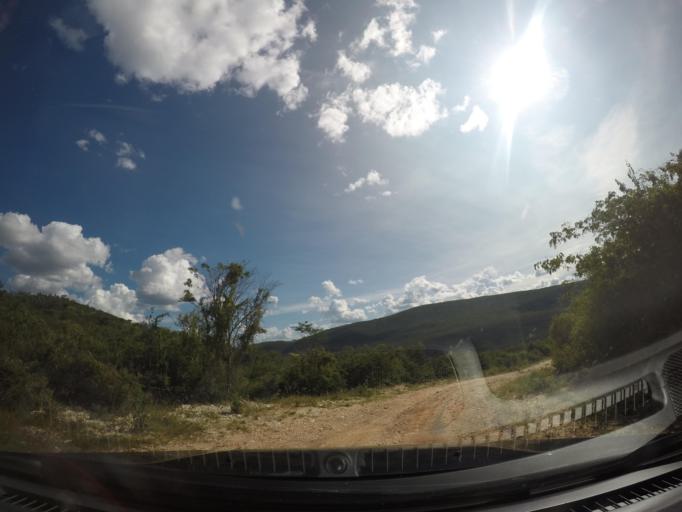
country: BR
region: Bahia
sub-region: Barra Da Estiva
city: Barra da Estiva
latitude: -13.2180
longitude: -41.5946
